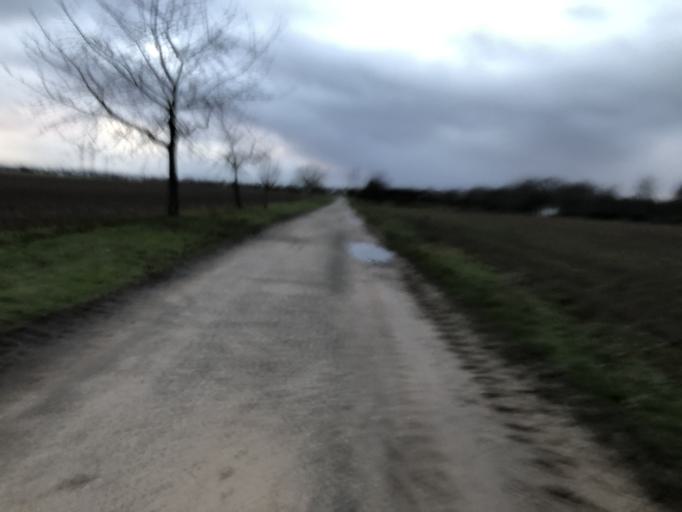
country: DE
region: Baden-Wuerttemberg
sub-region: Karlsruhe Region
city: Neulussheim
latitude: 49.3049
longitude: 8.5237
